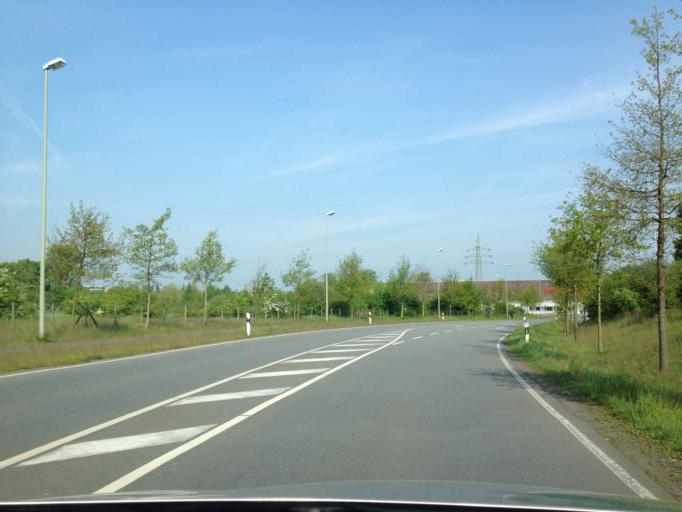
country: DE
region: North Rhine-Westphalia
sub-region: Regierungsbezirk Detmold
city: Guetersloh
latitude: 51.9097
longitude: 8.4270
